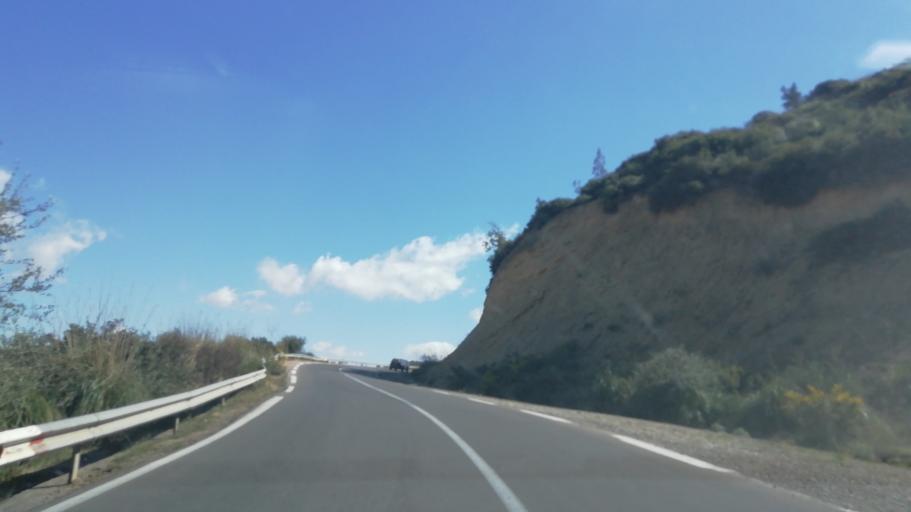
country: DZ
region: Mascara
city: Mascara
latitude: 35.4818
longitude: 0.1582
